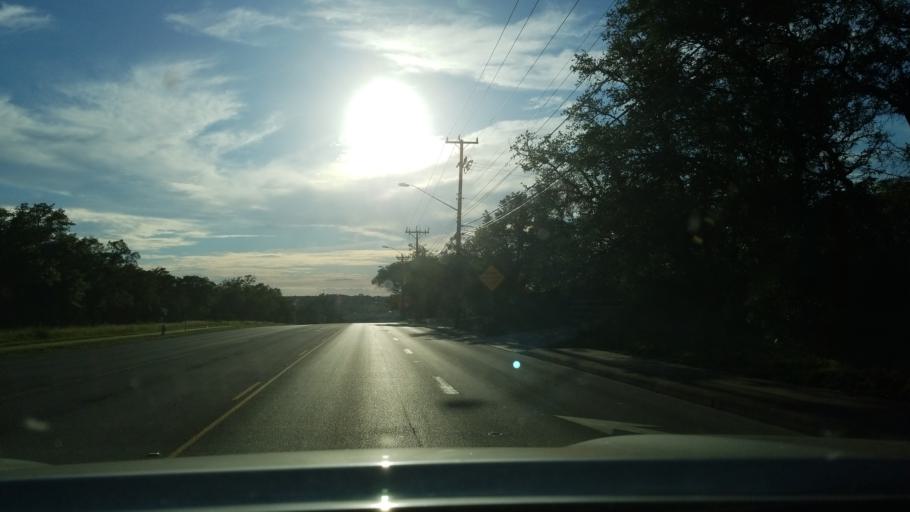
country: US
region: Texas
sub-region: Bexar County
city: Hollywood Park
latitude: 29.6204
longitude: -98.4611
